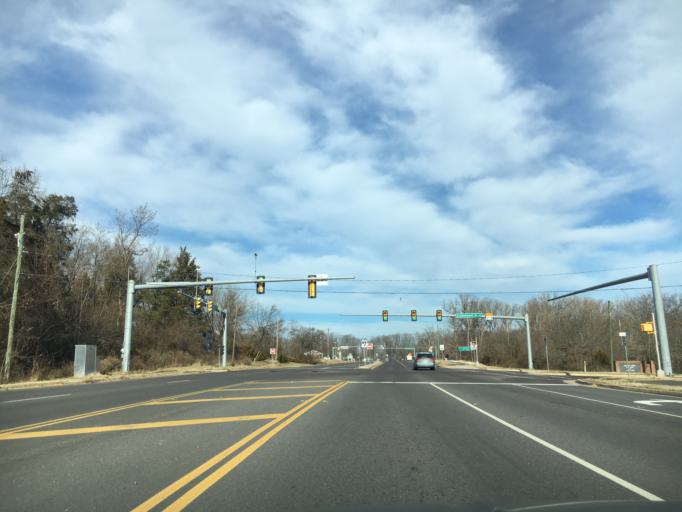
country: US
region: Virginia
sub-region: Culpeper County
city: Culpeper
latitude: 38.4964
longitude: -77.9922
